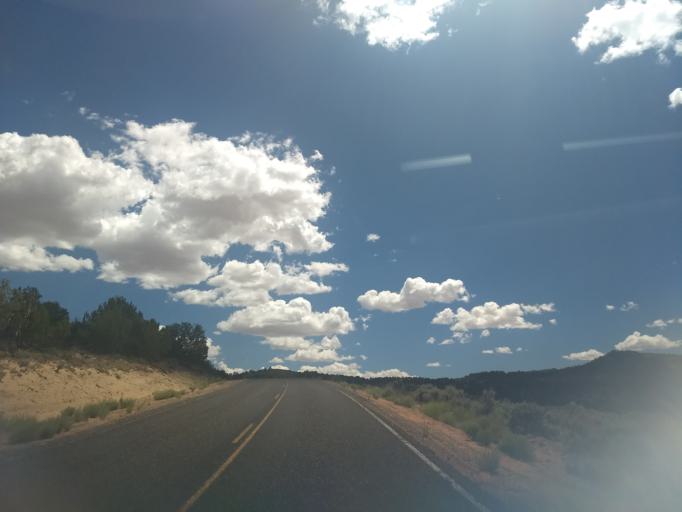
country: US
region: Utah
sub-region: Kane County
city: Kanab
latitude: 37.1266
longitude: -112.6788
